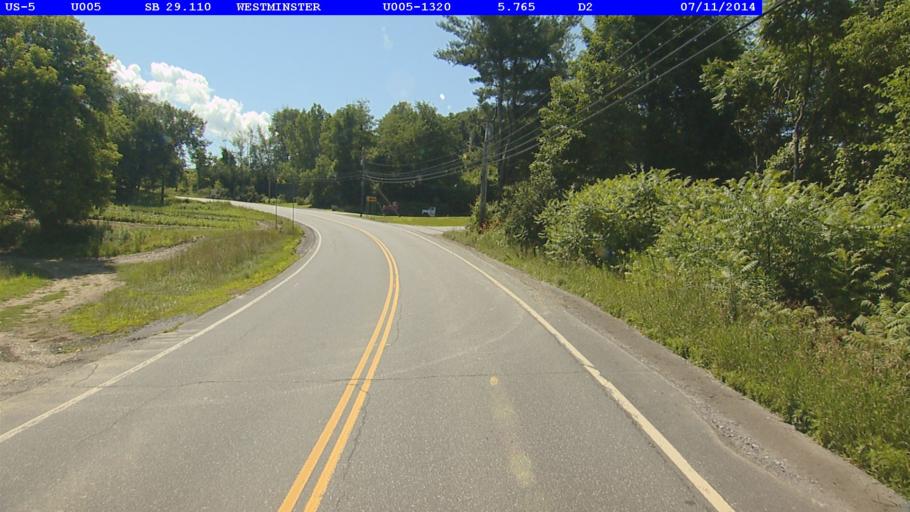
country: US
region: Vermont
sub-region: Windham County
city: Bellows Falls
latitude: 43.0927
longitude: -72.4434
